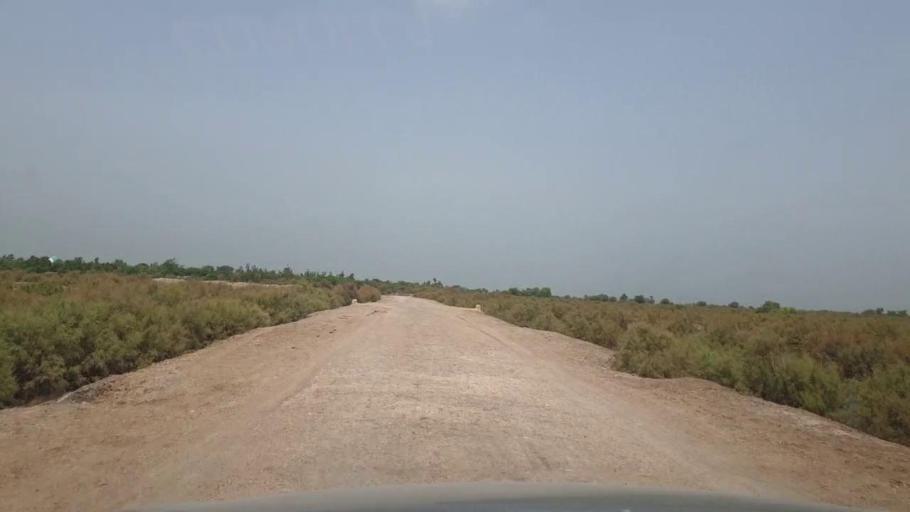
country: PK
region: Sindh
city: Garhi Yasin
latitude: 27.9174
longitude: 68.3771
